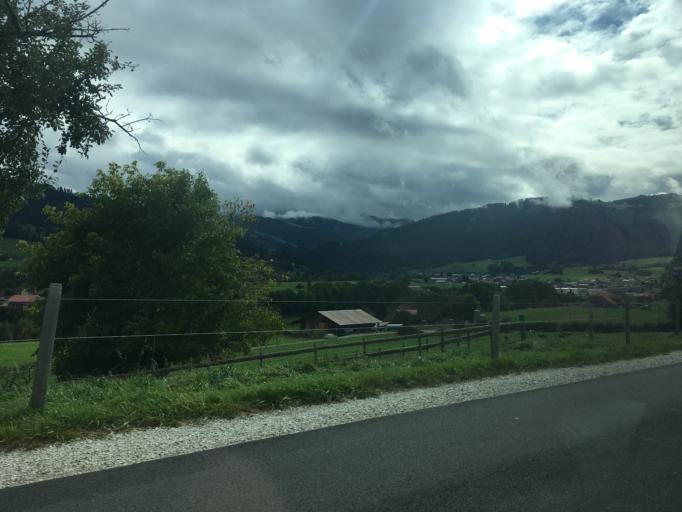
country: CH
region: Fribourg
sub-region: Sense District
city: Plaffeien
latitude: 46.7518
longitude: 7.2923
